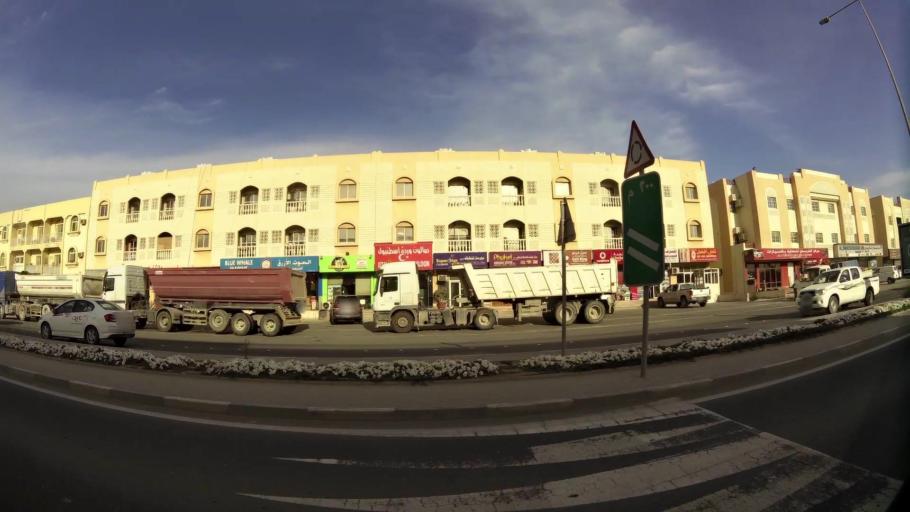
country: QA
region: Al Wakrah
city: Al Wakrah
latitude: 25.1635
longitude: 51.6075
